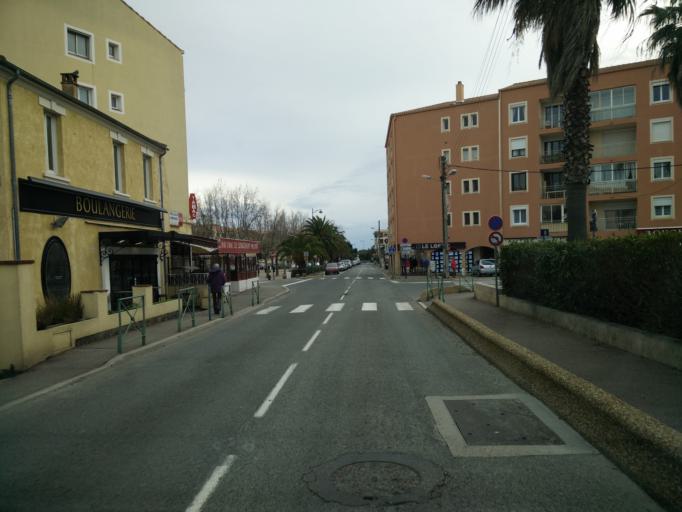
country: FR
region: Provence-Alpes-Cote d'Azur
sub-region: Departement du Var
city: Frejus
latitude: 43.3870
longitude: 6.7220
